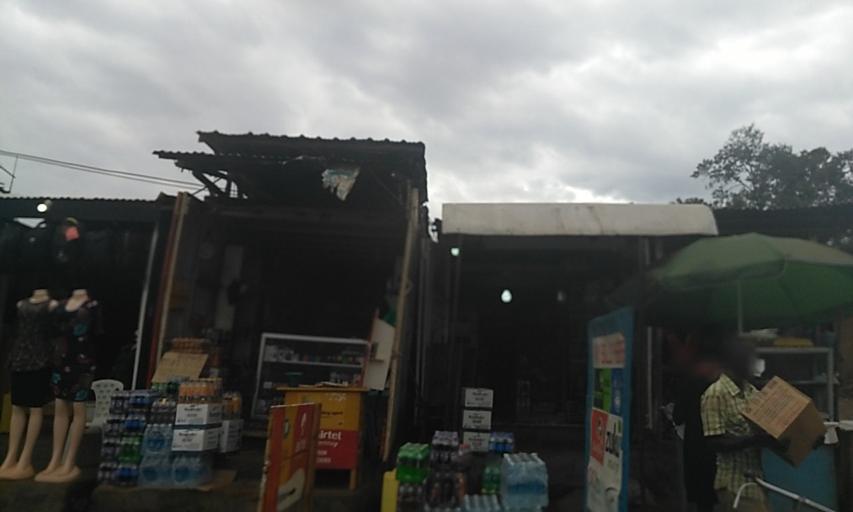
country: UG
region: Central Region
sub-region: Wakiso District
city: Bweyogerere
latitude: 0.3533
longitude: 32.6636
